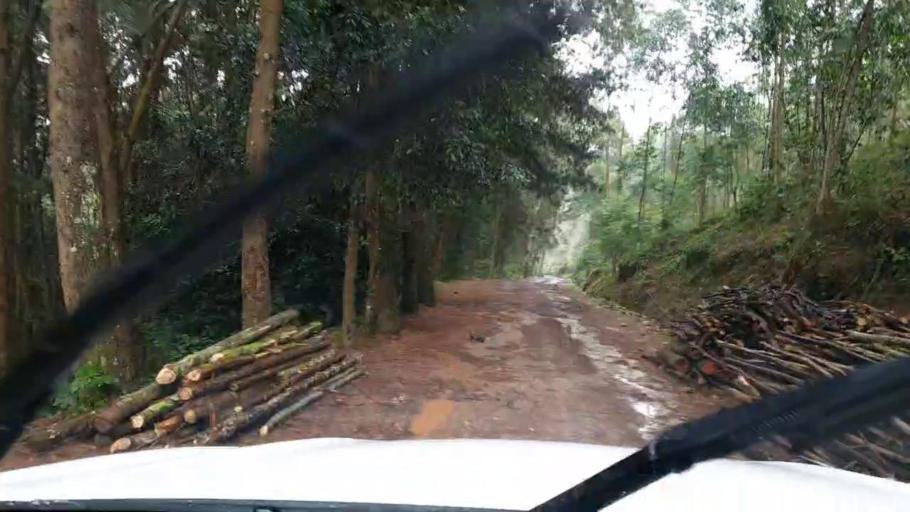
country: RW
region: Western Province
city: Cyangugu
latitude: -2.5519
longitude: 28.9774
